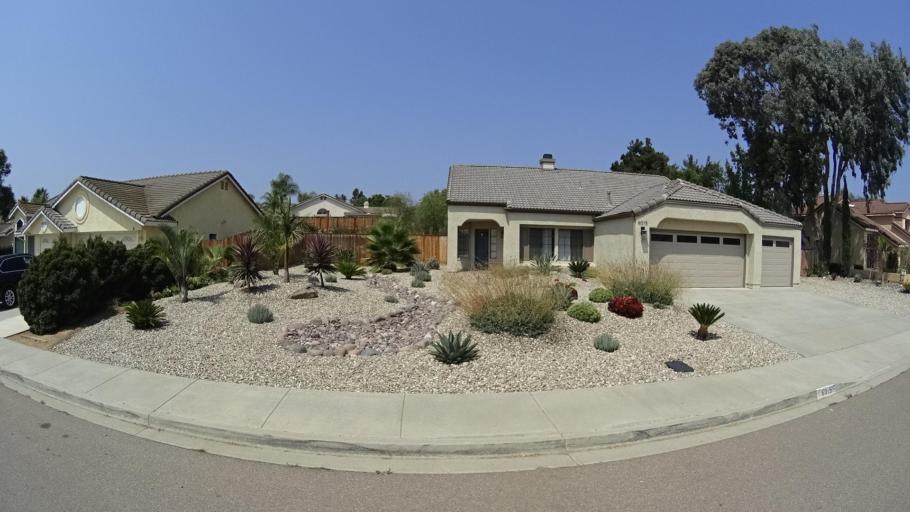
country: US
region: California
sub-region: San Diego County
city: Bonsall
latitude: 33.2936
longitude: -117.2257
